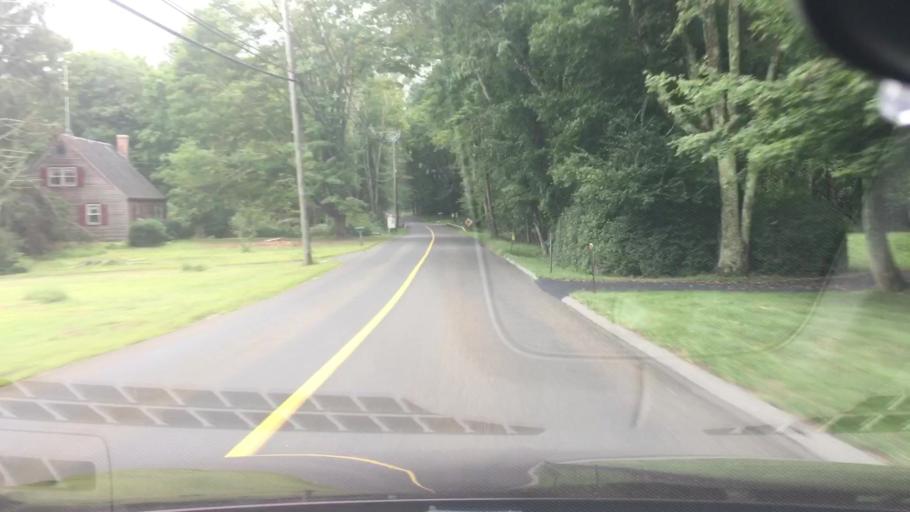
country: US
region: Connecticut
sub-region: New Haven County
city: Madison
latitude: 41.3369
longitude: -72.5798
